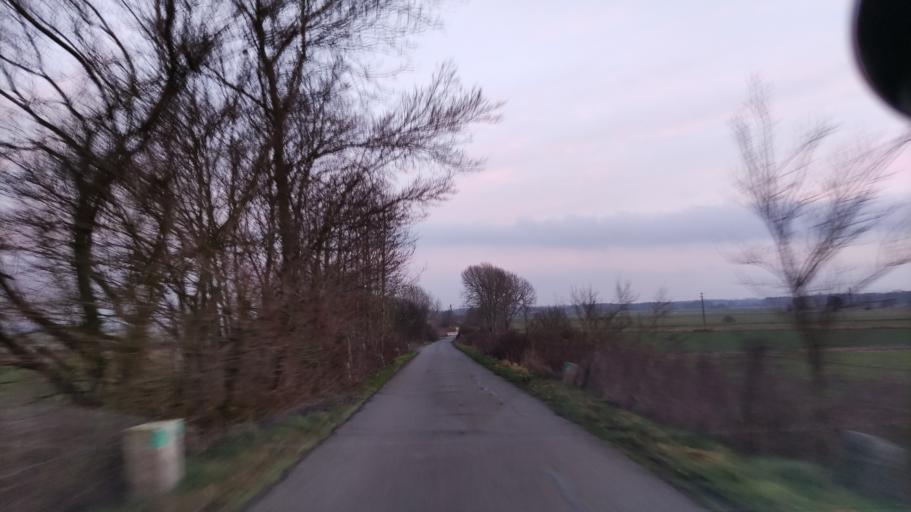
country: DE
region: Lower Saxony
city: Echem
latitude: 53.3384
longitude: 10.5009
